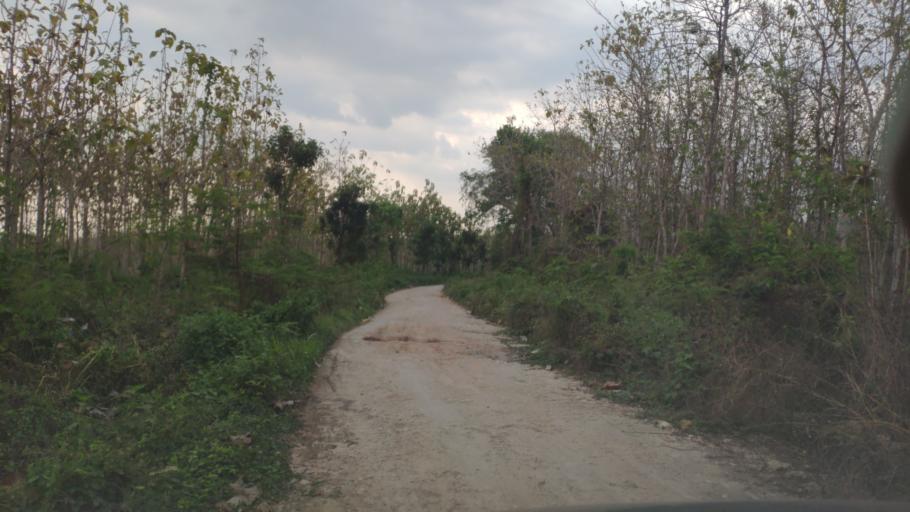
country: ID
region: Central Java
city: Randublatung
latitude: -7.2820
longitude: 111.2902
